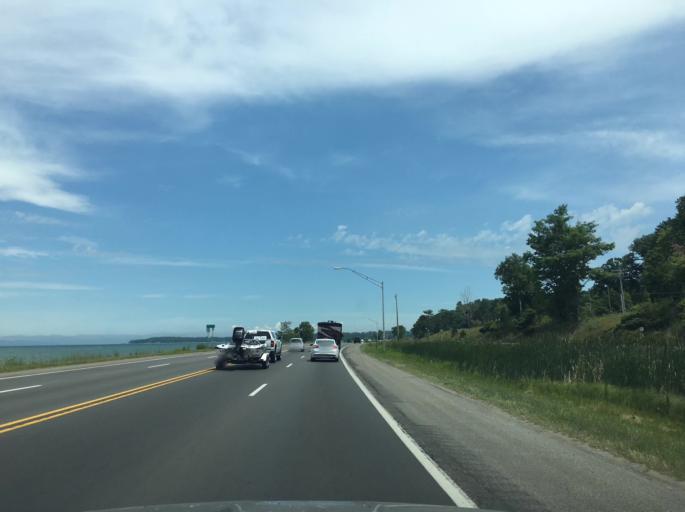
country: US
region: Michigan
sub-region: Grand Traverse County
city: Traverse City
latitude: 44.7544
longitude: -85.5210
